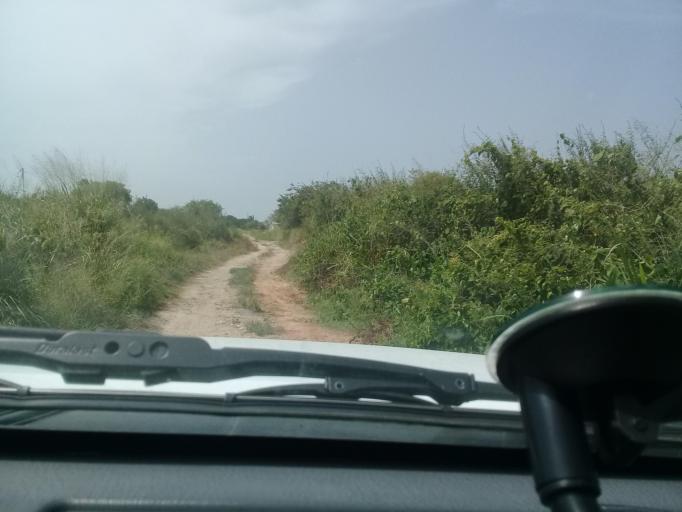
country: MX
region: Veracruz
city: Anahuac
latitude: 22.2170
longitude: -97.8265
